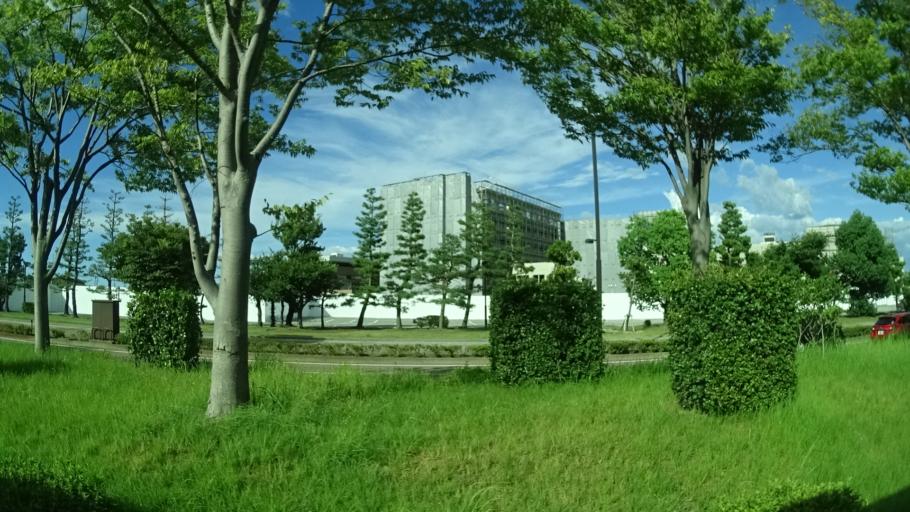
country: JP
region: Ishikawa
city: Kanazawa-shi
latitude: 36.5948
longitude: 136.6273
